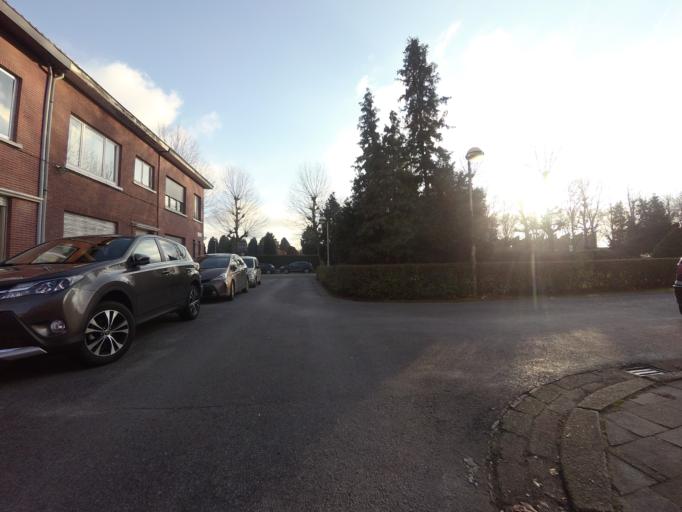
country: BE
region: Flanders
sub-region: Provincie Antwerpen
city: Hoboken
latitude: 51.1769
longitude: 4.3698
